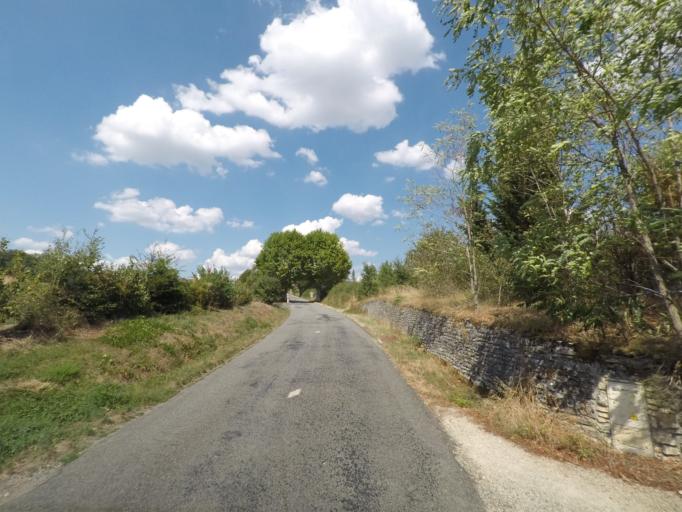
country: FR
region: Midi-Pyrenees
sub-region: Departement du Lot
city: Cahors
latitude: 44.5650
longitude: 1.5814
